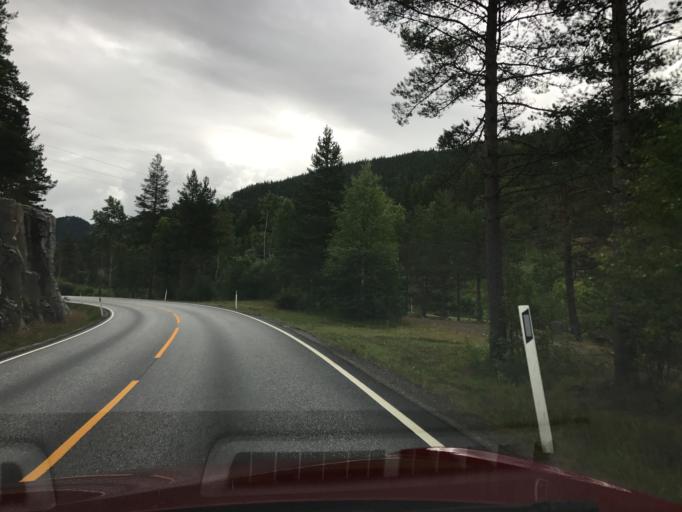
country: NO
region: Buskerud
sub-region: Nore og Uvdal
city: Rodberg
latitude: 60.2579
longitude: 8.9233
